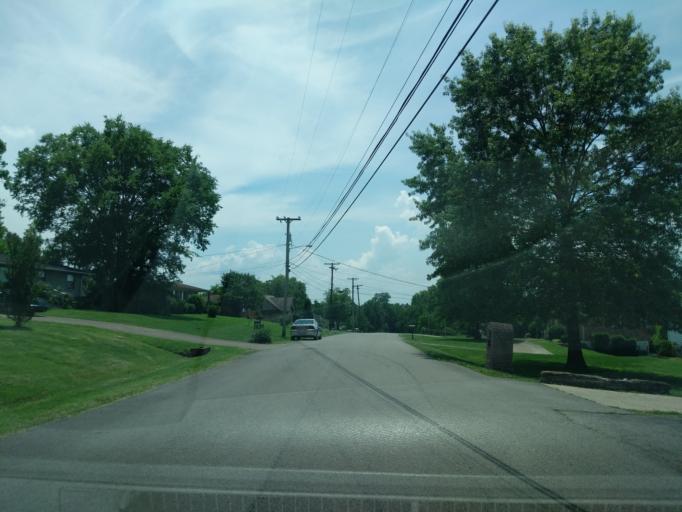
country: US
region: Tennessee
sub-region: Davidson County
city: Lakewood
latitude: 36.2365
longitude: -86.6320
